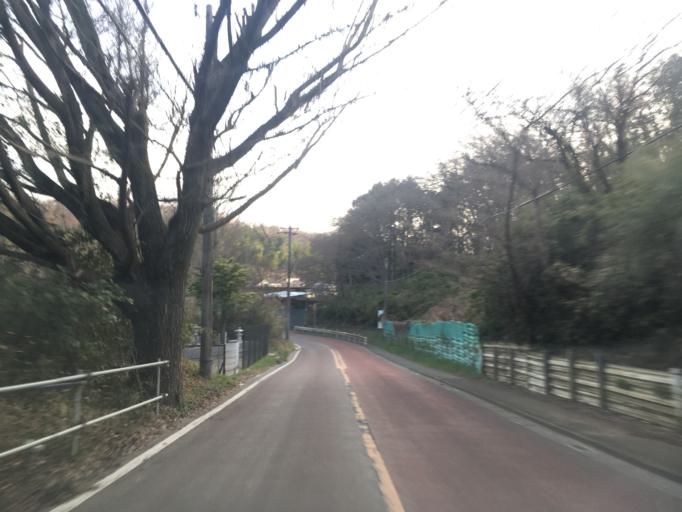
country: JP
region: Tokyo
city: Hino
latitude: 35.6426
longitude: 139.3946
